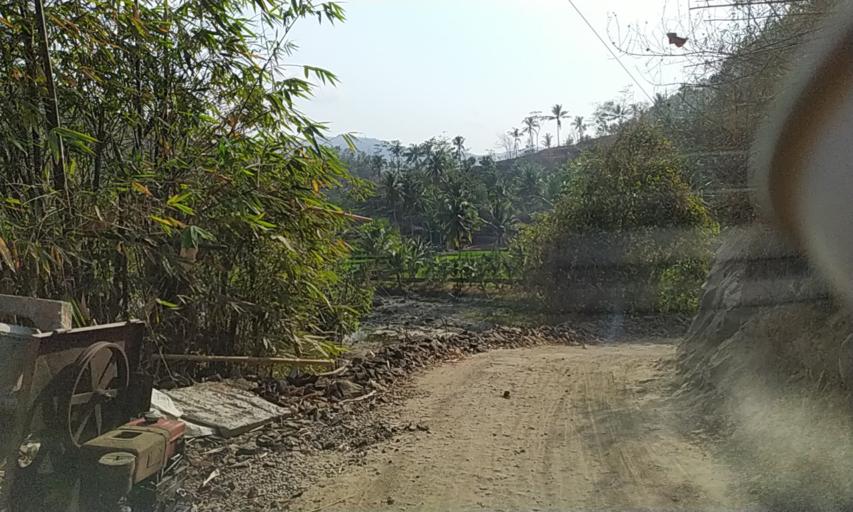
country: ID
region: Central Java
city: Bantarmangu
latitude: -7.3315
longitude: 108.8675
